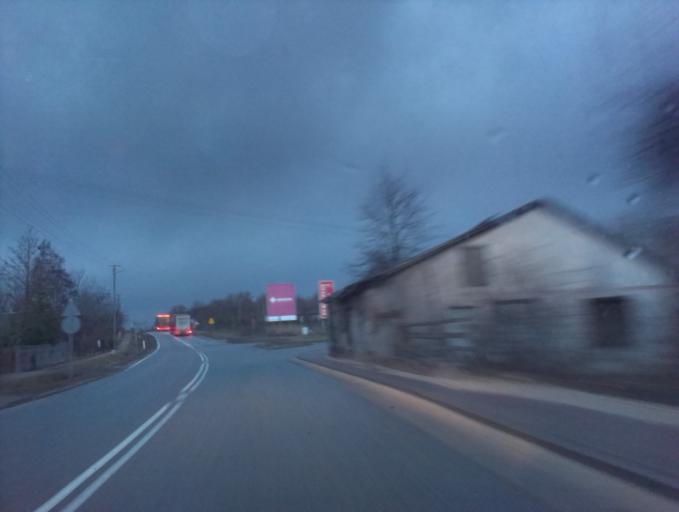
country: PL
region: Lodz Voivodeship
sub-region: Powiat opoczynski
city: Zarnow
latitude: 51.2510
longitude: 20.1712
